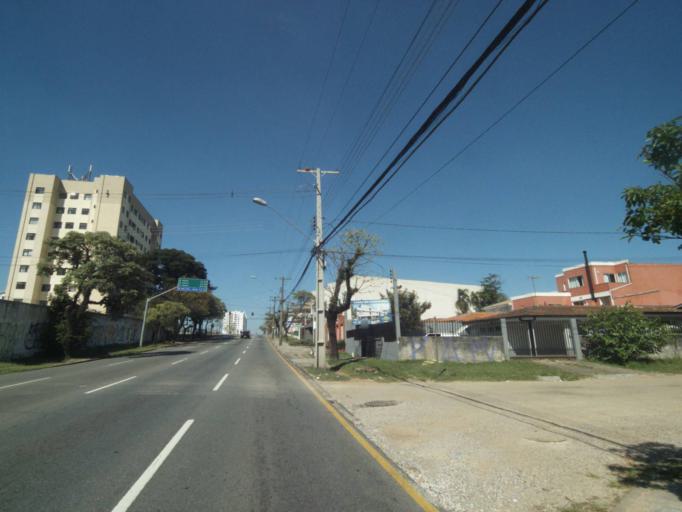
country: BR
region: Parana
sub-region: Curitiba
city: Curitiba
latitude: -25.3837
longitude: -49.2329
